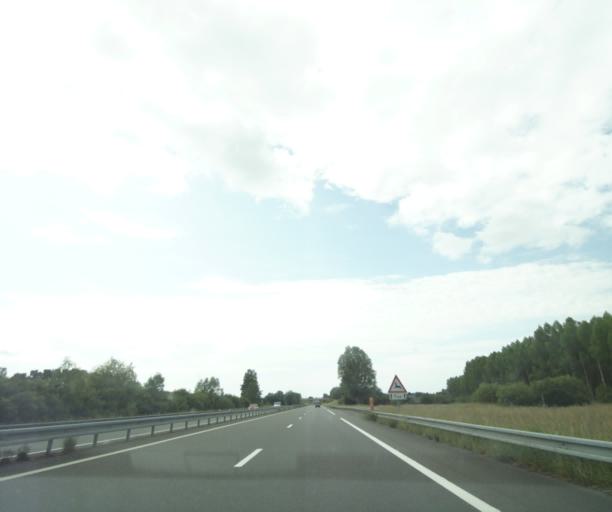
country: FR
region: Pays de la Loire
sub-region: Departement de Maine-et-Loire
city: Beaufort-en-Vallee
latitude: 47.4800
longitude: -0.2086
